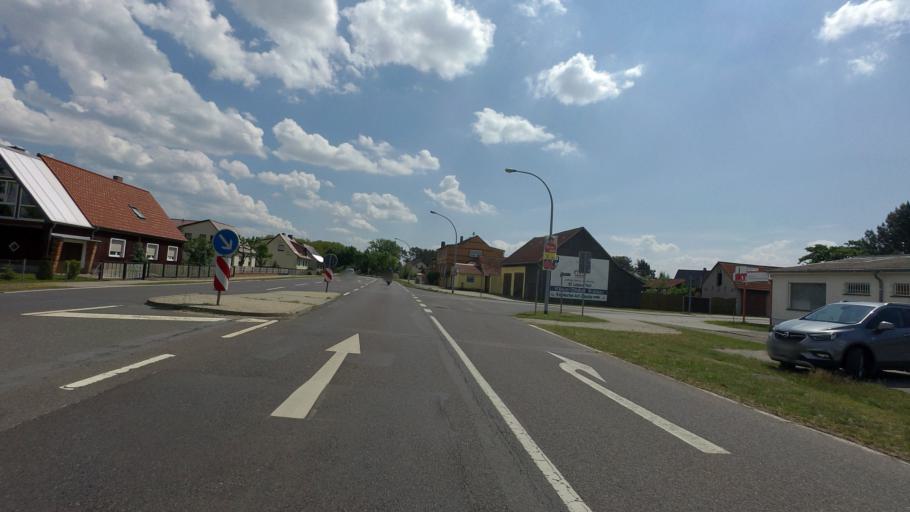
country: DE
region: Brandenburg
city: Lubbenau
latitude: 51.9436
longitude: 13.9885
